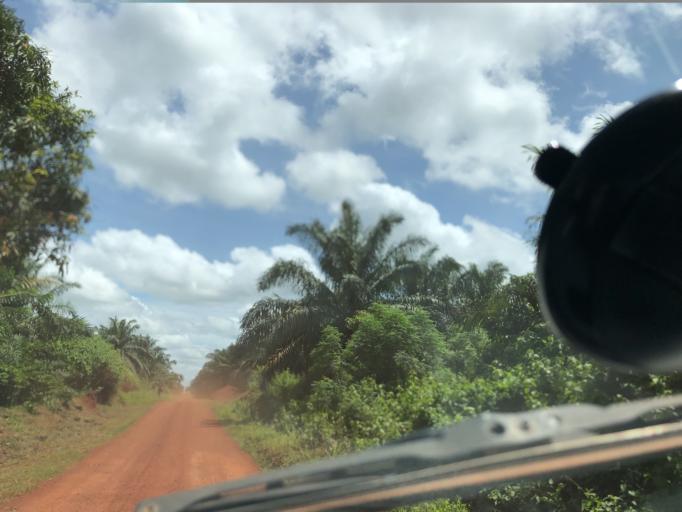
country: CD
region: Equateur
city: Gemena
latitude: 3.5351
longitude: 19.3494
